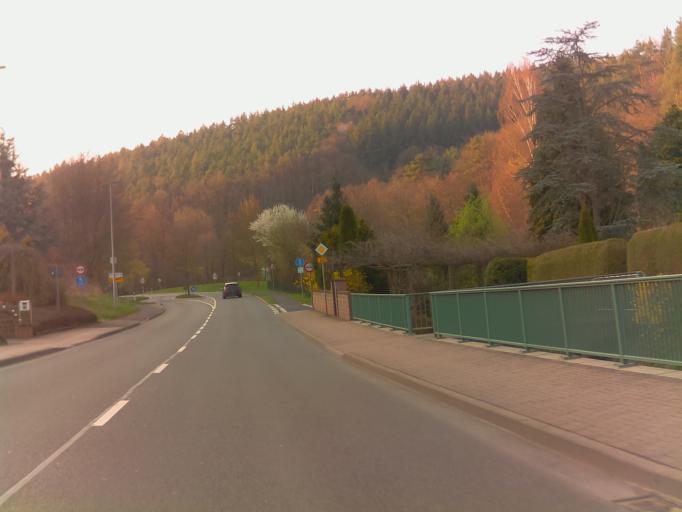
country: DE
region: Thuringia
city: Unterbreizbach
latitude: 50.8570
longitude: 9.9458
